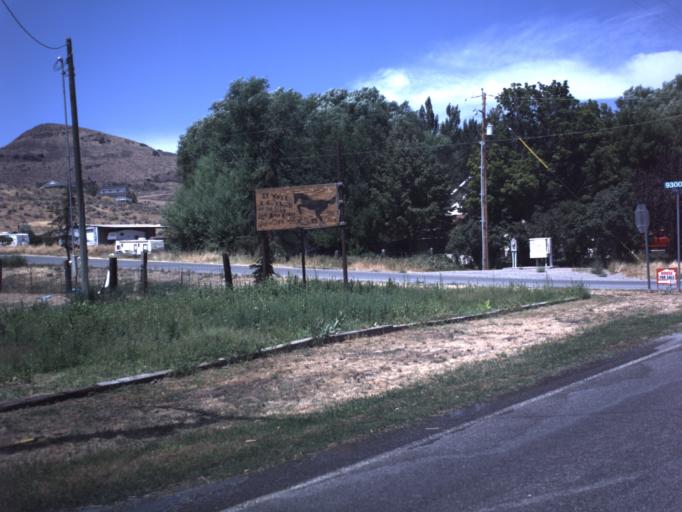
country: US
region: Utah
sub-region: Box Elder County
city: Tremonton
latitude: 41.6730
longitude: -112.2966
